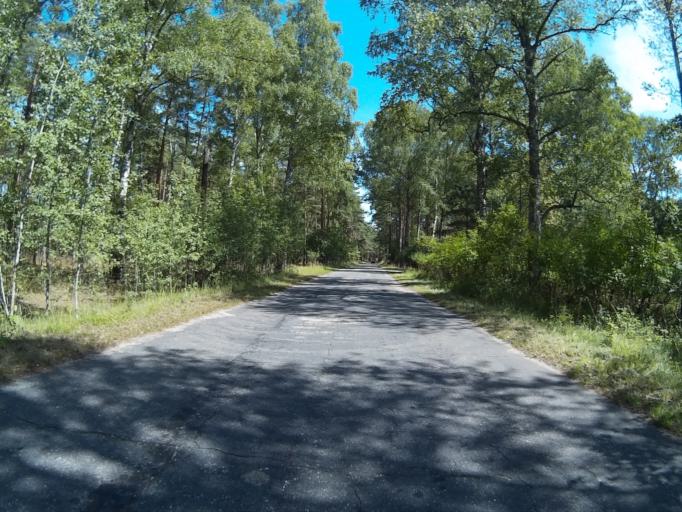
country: PL
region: Pomeranian Voivodeship
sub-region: Powiat chojnicki
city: Czersk
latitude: 53.6829
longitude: 17.9827
